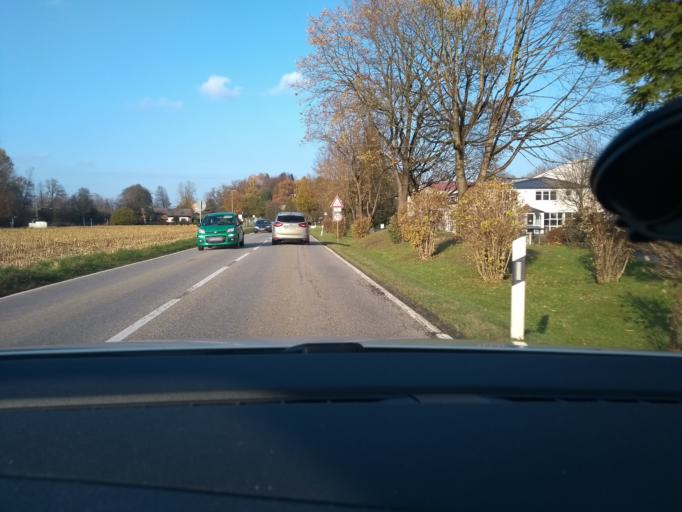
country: DE
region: Bavaria
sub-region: Upper Bavaria
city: Rohrdorf
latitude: 47.8287
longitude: 12.1549
